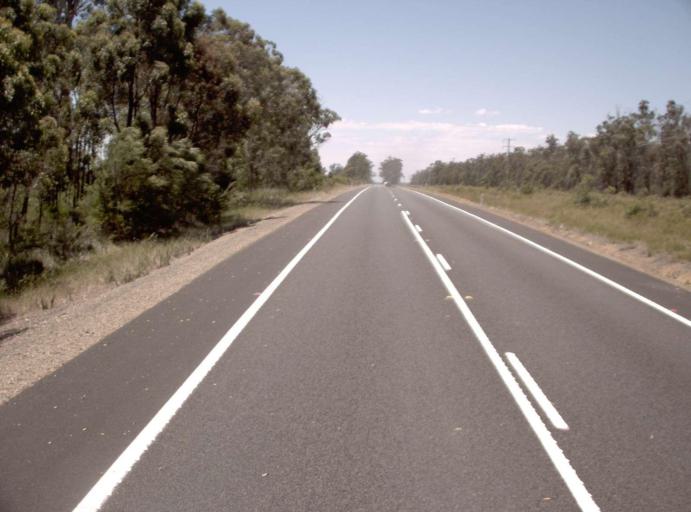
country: AU
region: Victoria
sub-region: East Gippsland
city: Lakes Entrance
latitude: -37.7549
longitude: 148.3128
